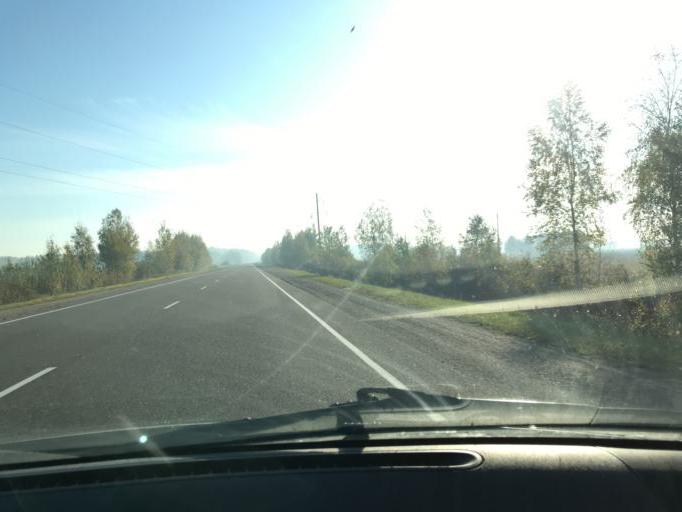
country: BY
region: Brest
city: Horad Luninyets
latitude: 52.3126
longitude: 26.6581
